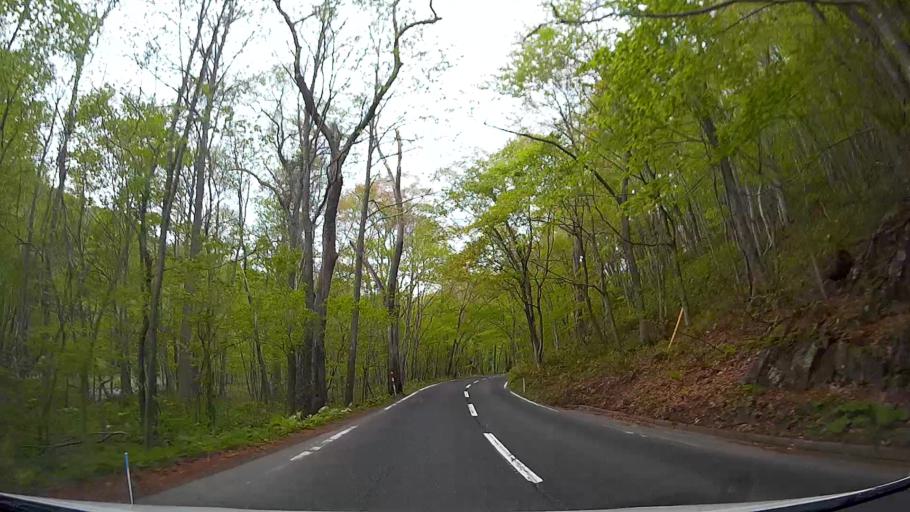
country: JP
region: Aomori
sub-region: Aomori Shi
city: Furudate
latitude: 40.5716
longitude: 140.9786
